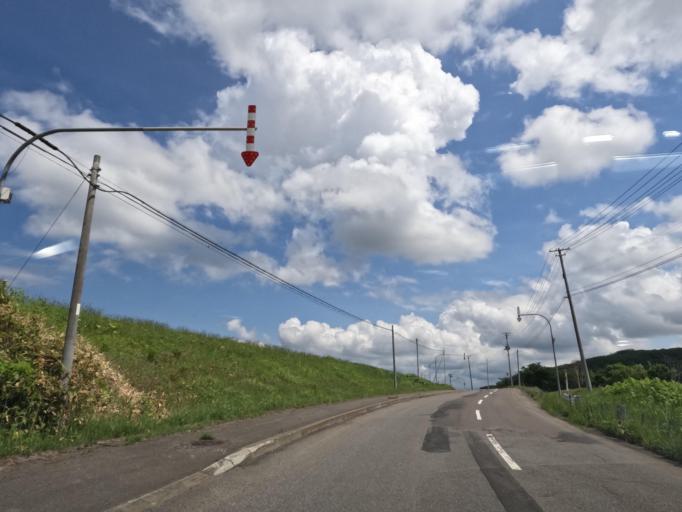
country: JP
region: Hokkaido
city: Takikawa
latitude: 43.5851
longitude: 141.8027
